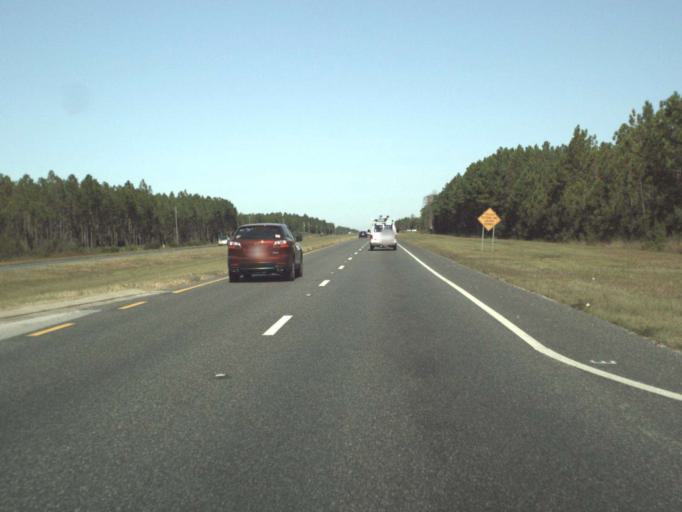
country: US
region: Florida
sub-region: Bay County
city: Laguna Beach
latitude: 30.2905
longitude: -86.0195
